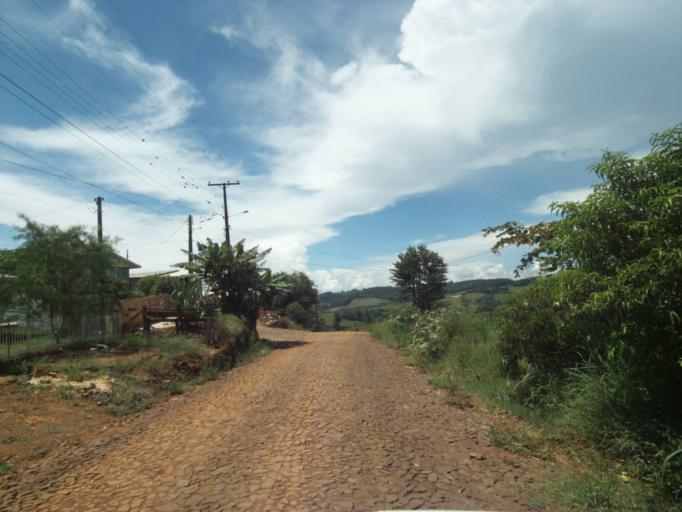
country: BR
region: Parana
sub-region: Guaraniacu
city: Guaraniacu
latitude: -25.0911
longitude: -52.8735
